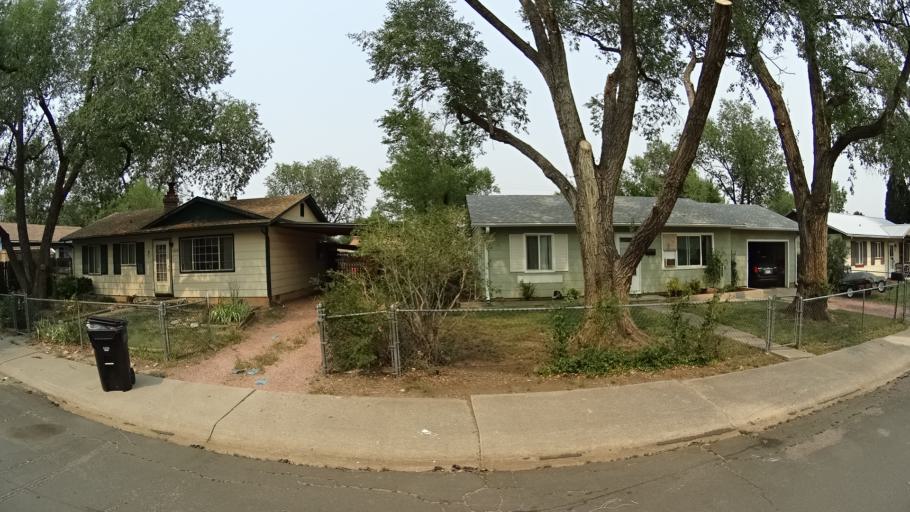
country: US
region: Colorado
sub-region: El Paso County
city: Stratmoor
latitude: 38.7968
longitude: -104.8059
